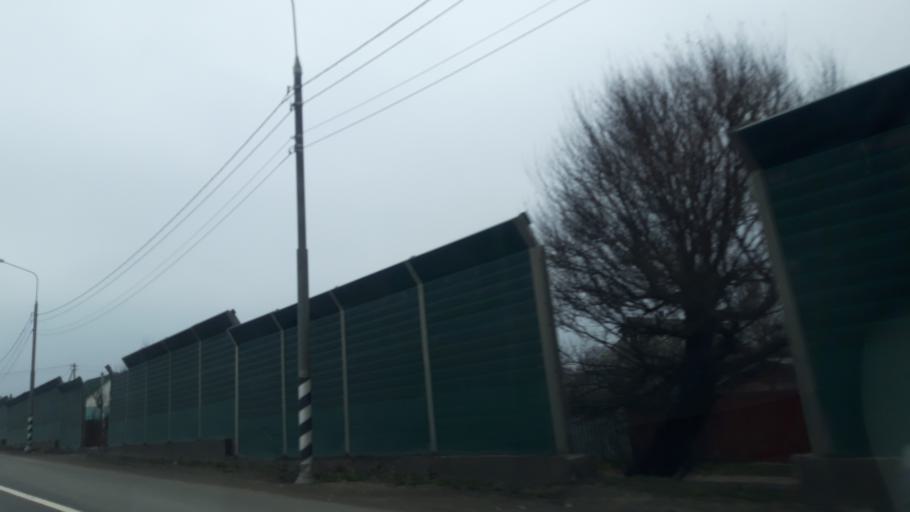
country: RU
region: Moskovskaya
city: Peshki
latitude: 56.1267
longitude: 37.0732
